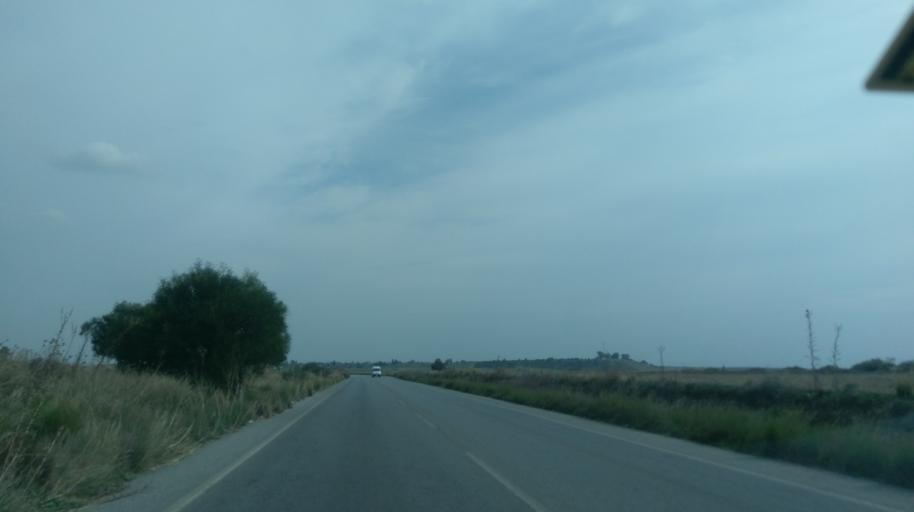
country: CY
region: Ammochostos
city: Lefkonoiko
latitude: 35.2616
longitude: 33.7583
